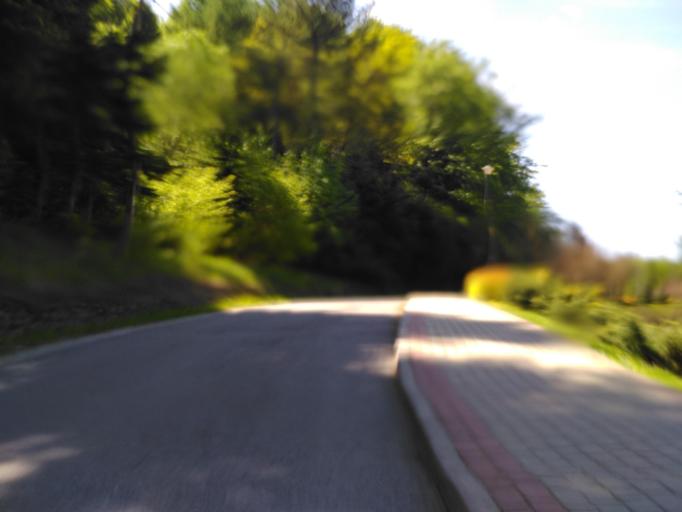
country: PL
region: Subcarpathian Voivodeship
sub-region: Powiat krosnienski
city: Iwonicz-Zdroj
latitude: 49.5578
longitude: 21.7874
